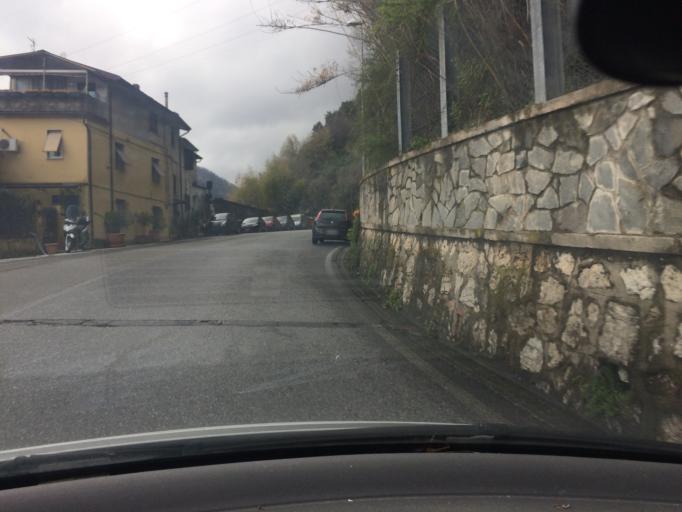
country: IT
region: Tuscany
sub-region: Provincia di Massa-Carrara
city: Massa
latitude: 44.0510
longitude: 10.1280
